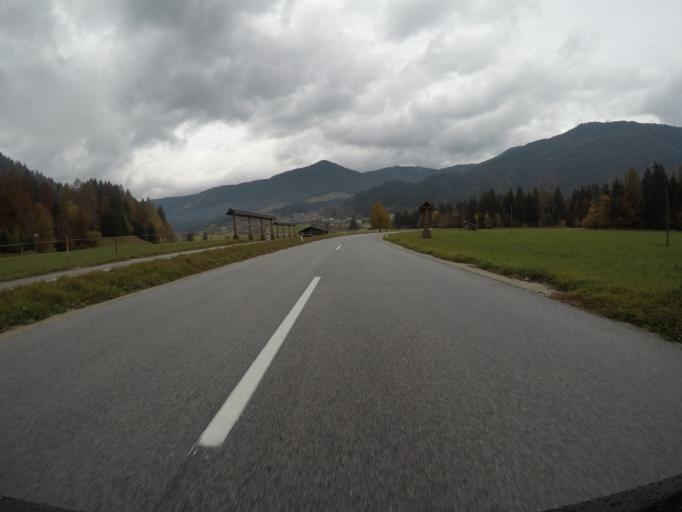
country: AT
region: Carinthia
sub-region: Politischer Bezirk Villach Land
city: Arnoldstein
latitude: 46.4877
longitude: 13.7242
